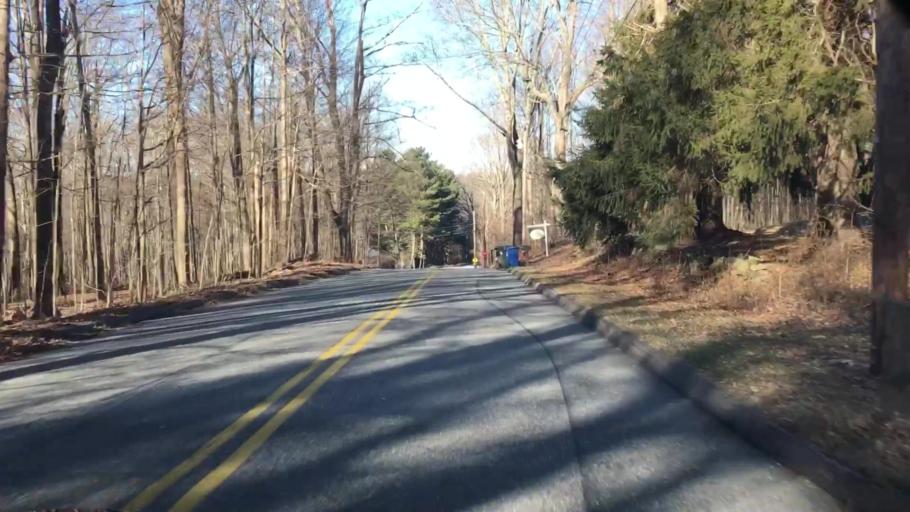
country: US
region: Connecticut
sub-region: Tolland County
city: Tolland
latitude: 41.8969
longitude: -72.3912
